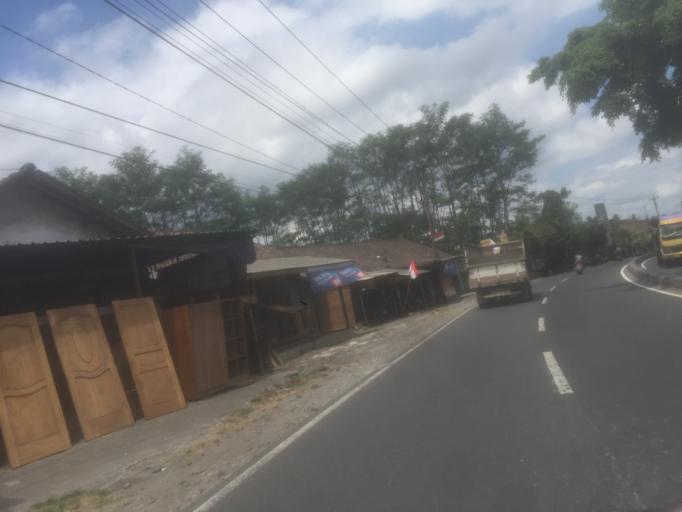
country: ID
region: Central Java
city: Muntilan
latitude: -7.6290
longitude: 110.3215
